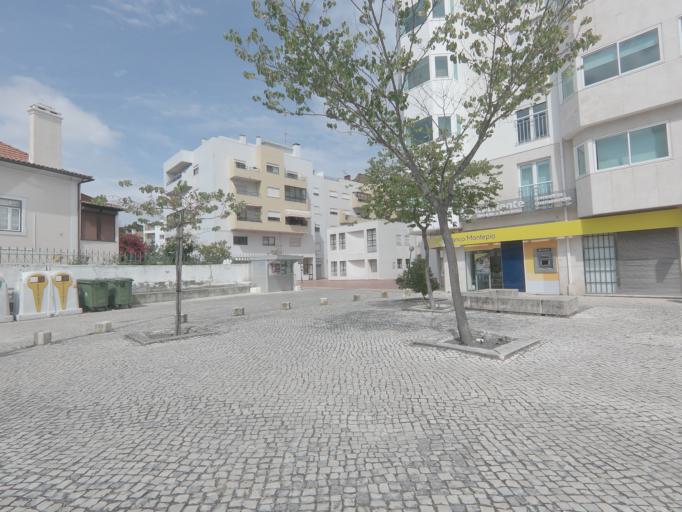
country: PT
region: Leiria
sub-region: Leiria
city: Leiria
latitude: 39.7397
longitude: -8.8091
